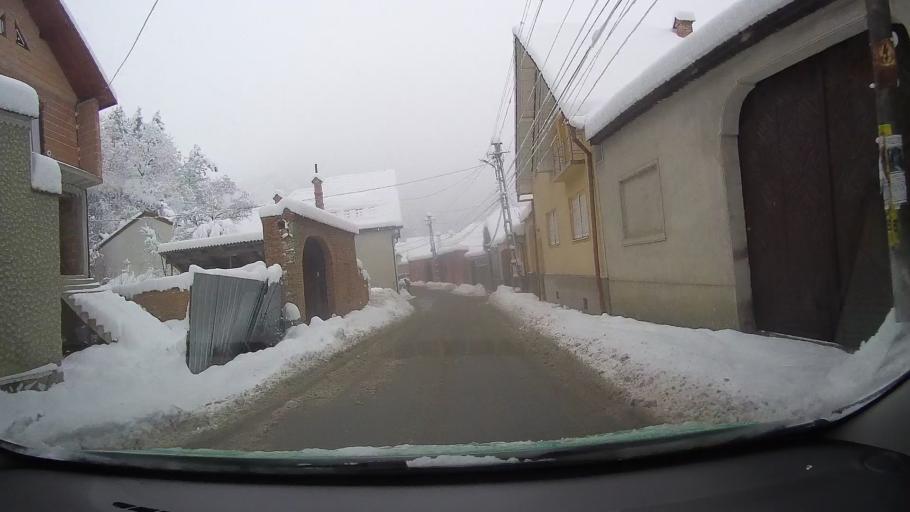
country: RO
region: Sibiu
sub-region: Comuna Tilisca
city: Tilisca
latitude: 45.8011
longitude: 23.8396
